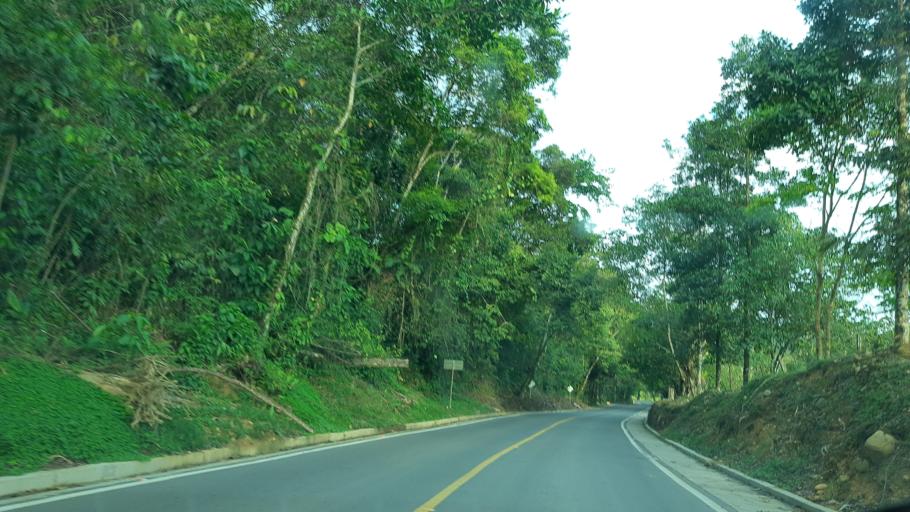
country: CO
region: Boyaca
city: San Luis de Gaceno
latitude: 4.8163
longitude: -73.1798
